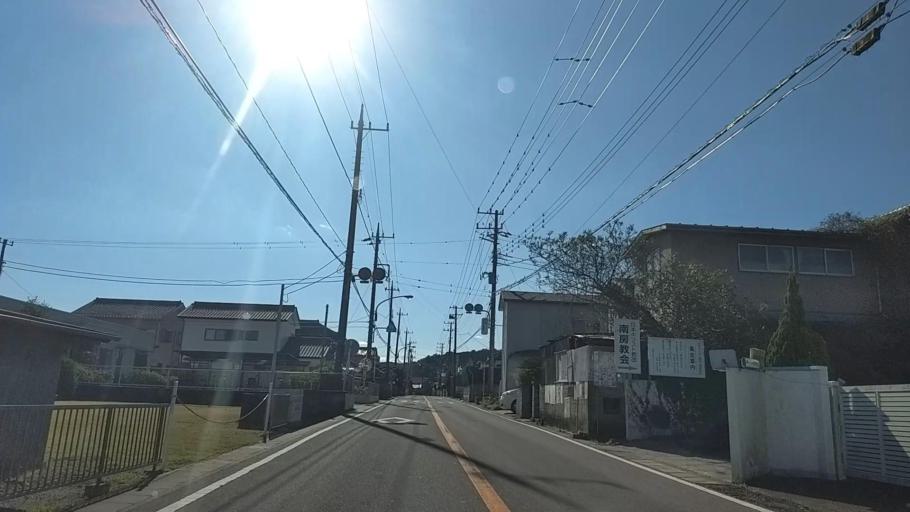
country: JP
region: Chiba
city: Tateyama
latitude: 34.9797
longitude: 139.8632
